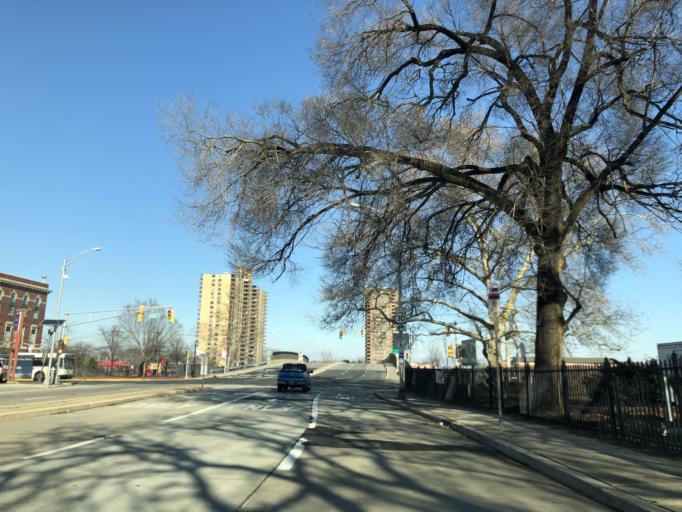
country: US
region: New Jersey
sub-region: Camden County
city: Camden
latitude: 39.9455
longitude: -75.1167
